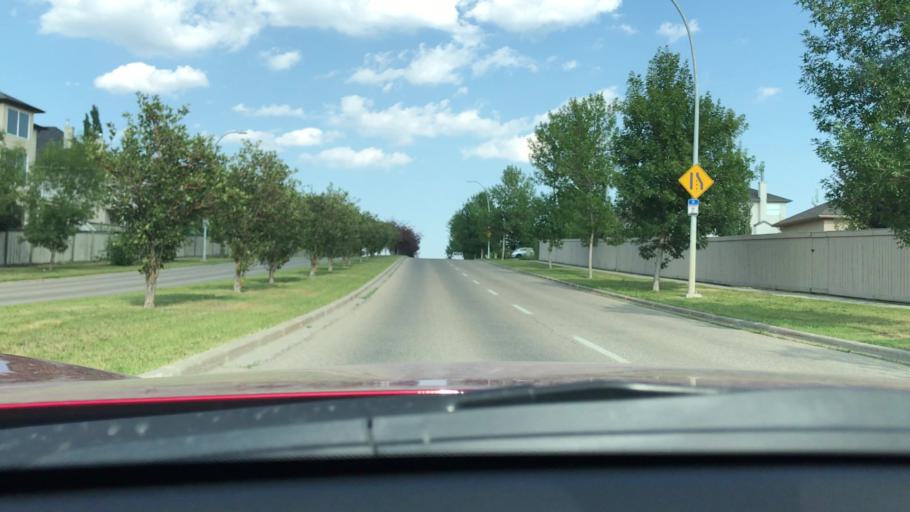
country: CA
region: Alberta
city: Calgary
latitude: 51.0305
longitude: -114.1804
